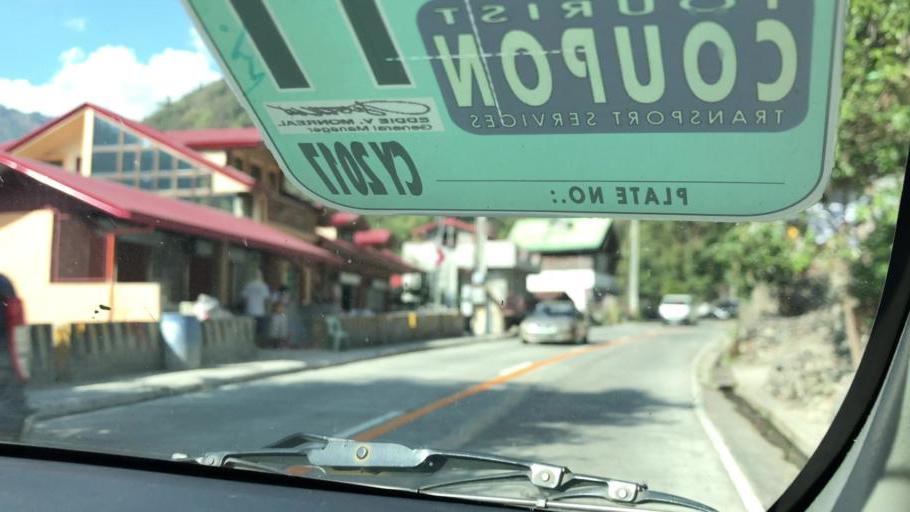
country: PH
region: Cordillera
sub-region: Province of Benguet
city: Tuba
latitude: 16.3152
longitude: 120.6180
